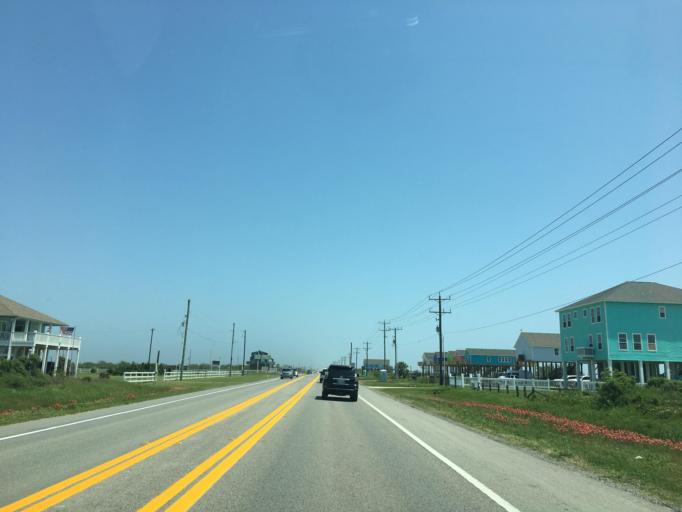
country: US
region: Texas
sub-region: Galveston County
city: Bolivar Peninsula
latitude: 29.5052
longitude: -94.5089
